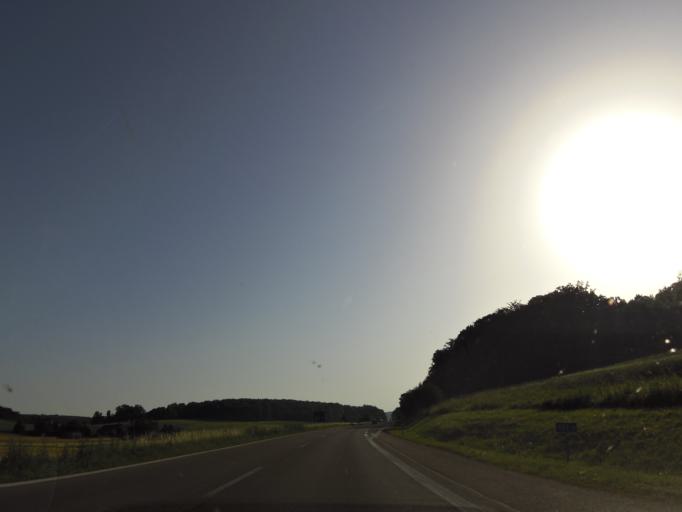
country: DE
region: Baden-Wuerttemberg
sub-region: Regierungsbezirk Stuttgart
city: Hohenstadt
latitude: 48.5506
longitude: 9.6511
